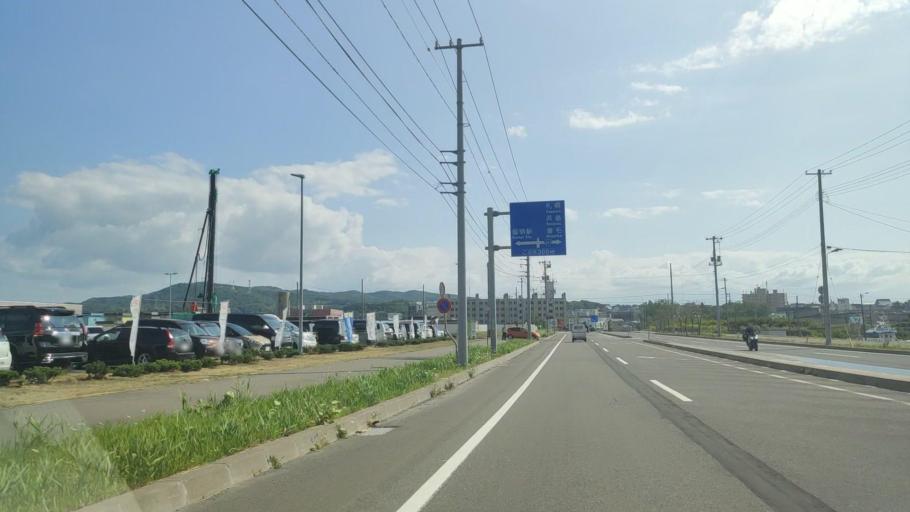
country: JP
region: Hokkaido
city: Rumoi
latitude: 43.9450
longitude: 141.6481
